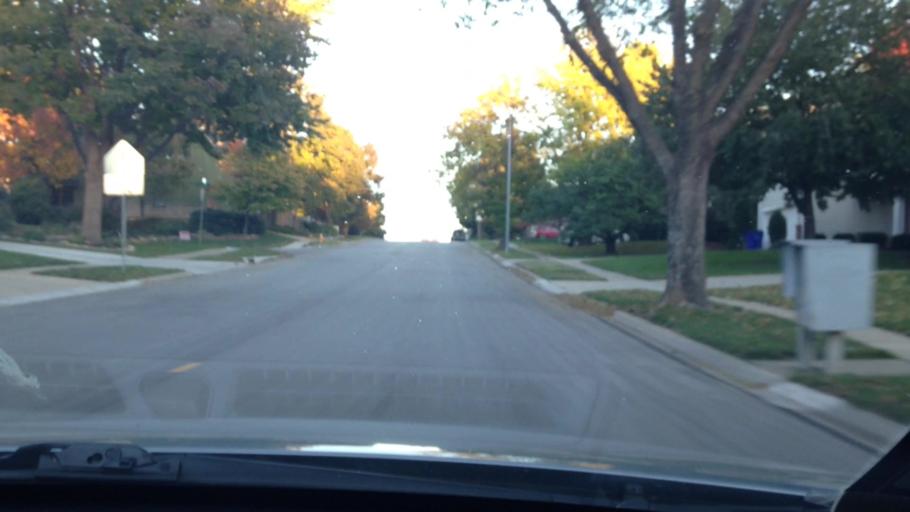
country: US
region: Kansas
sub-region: Johnson County
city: Lenexa
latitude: 38.9059
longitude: -94.7505
